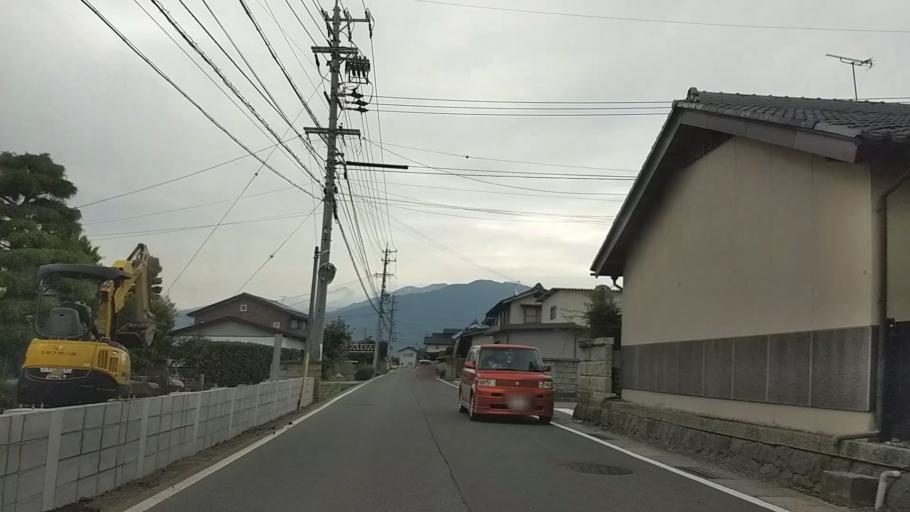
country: JP
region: Nagano
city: Nagano-shi
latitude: 36.6078
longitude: 138.2156
